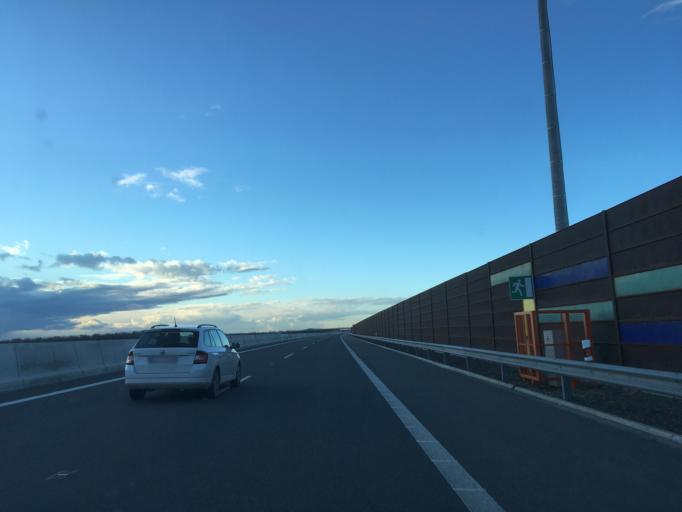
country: SK
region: Trnavsky
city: Samorin
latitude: 48.0256
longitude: 17.3848
